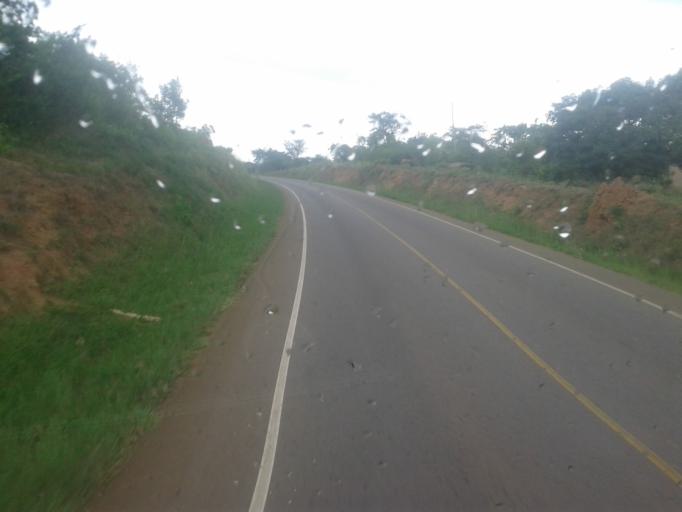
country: UG
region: Central Region
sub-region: Nakasongola District
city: Nakasongola
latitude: 1.3245
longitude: 32.4221
